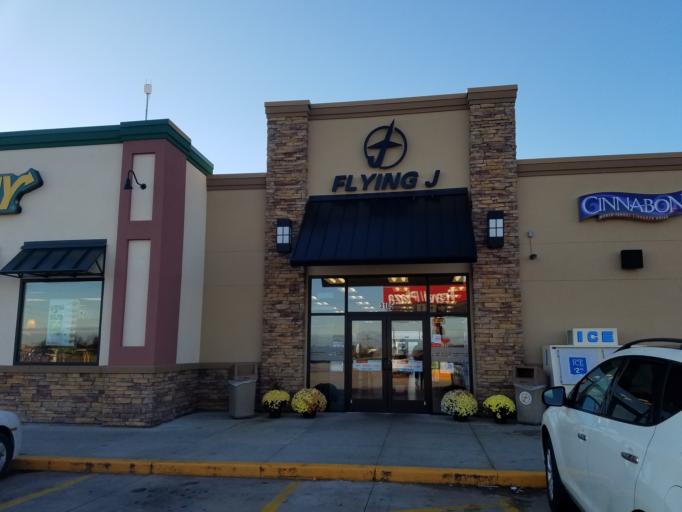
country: US
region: Indiana
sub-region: Allen County
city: New Haven
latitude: 41.0598
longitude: -84.9802
